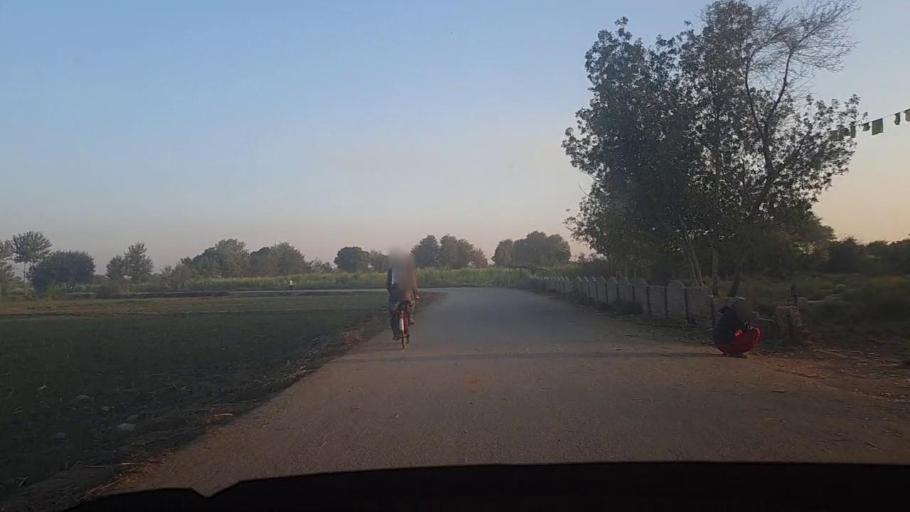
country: PK
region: Sindh
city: Sobhadero
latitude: 27.3527
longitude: 68.3719
